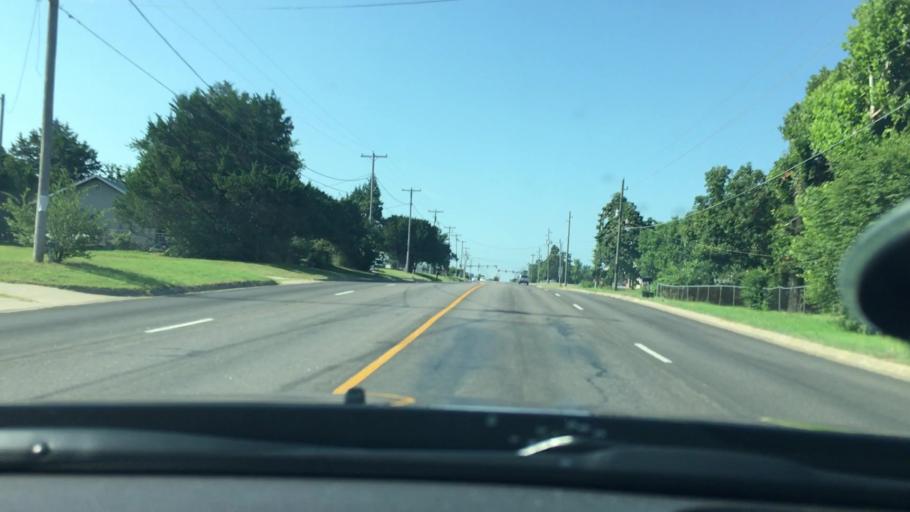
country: US
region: Oklahoma
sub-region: Pontotoc County
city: Ada
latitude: 34.7851
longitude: -96.6349
